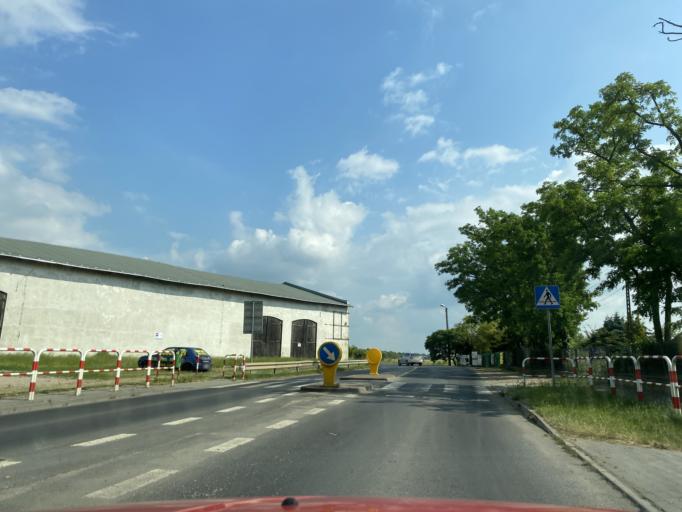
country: PL
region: Greater Poland Voivodeship
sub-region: Powiat poznanski
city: Dopiewo
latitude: 52.3596
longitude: 16.7105
